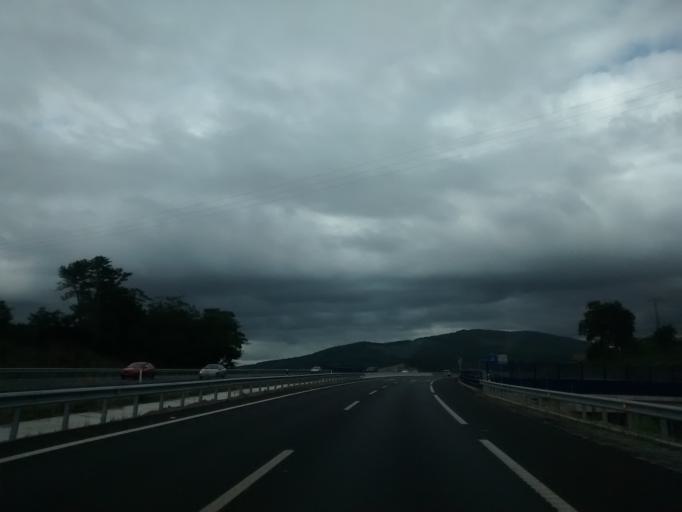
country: ES
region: Cantabria
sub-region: Provincia de Cantabria
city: Polanco
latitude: 43.3458
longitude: -3.9998
